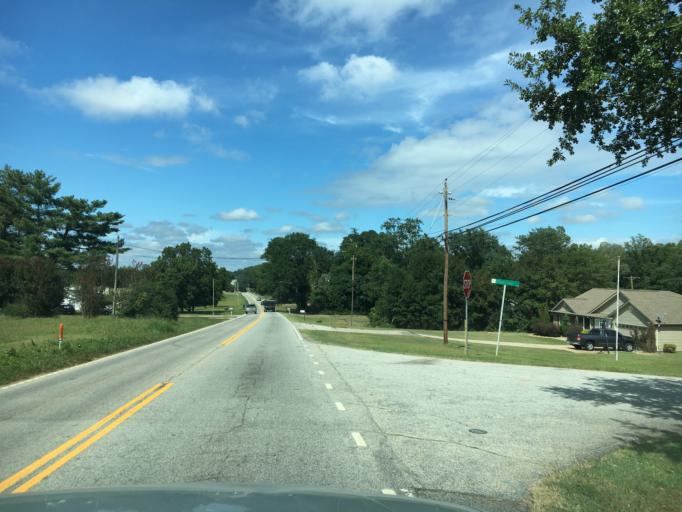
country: US
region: South Carolina
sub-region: Spartanburg County
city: Lyman
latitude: 34.9652
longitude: -82.1223
